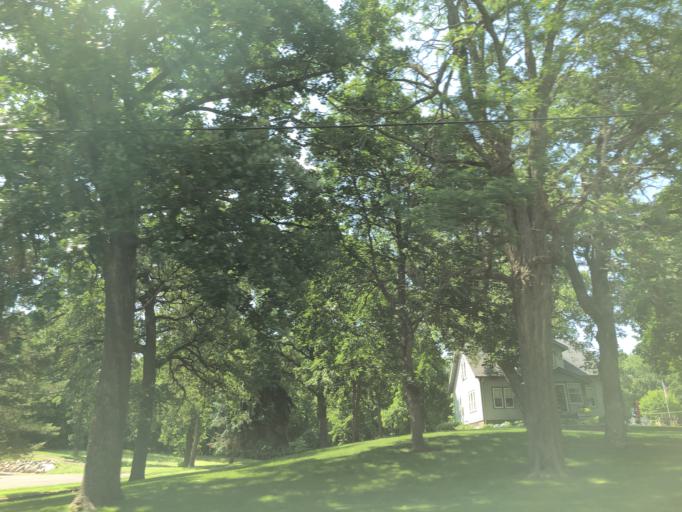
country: US
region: Minnesota
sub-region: Douglas County
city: Alexandria
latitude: 45.9356
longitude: -95.3826
